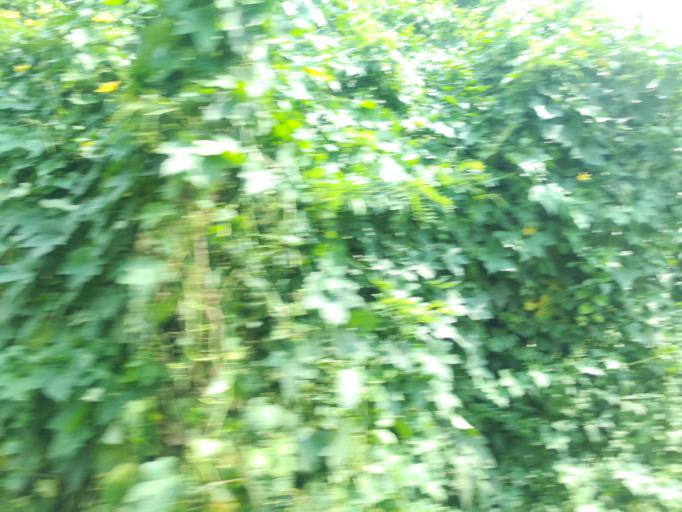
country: NG
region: Oyo
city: Ibadan
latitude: 7.4196
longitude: 3.8580
